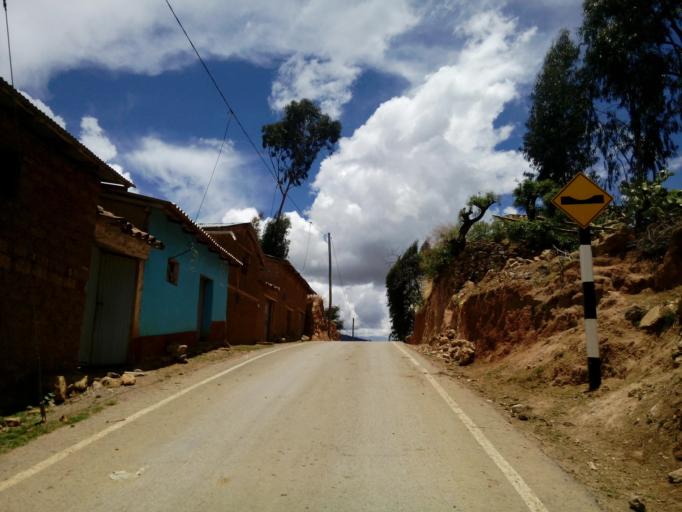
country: PE
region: Ayacucho
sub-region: Provincia de Victor Fajardo
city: Canaria
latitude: -13.8782
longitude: -73.9332
